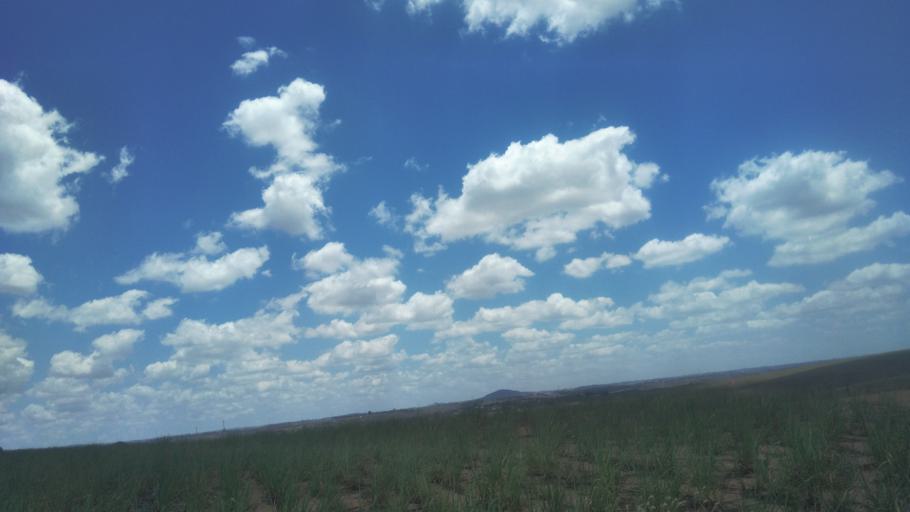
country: BR
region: Pernambuco
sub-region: Nazare Da Mata
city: Nazare da Mata
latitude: -7.7271
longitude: -35.2415
